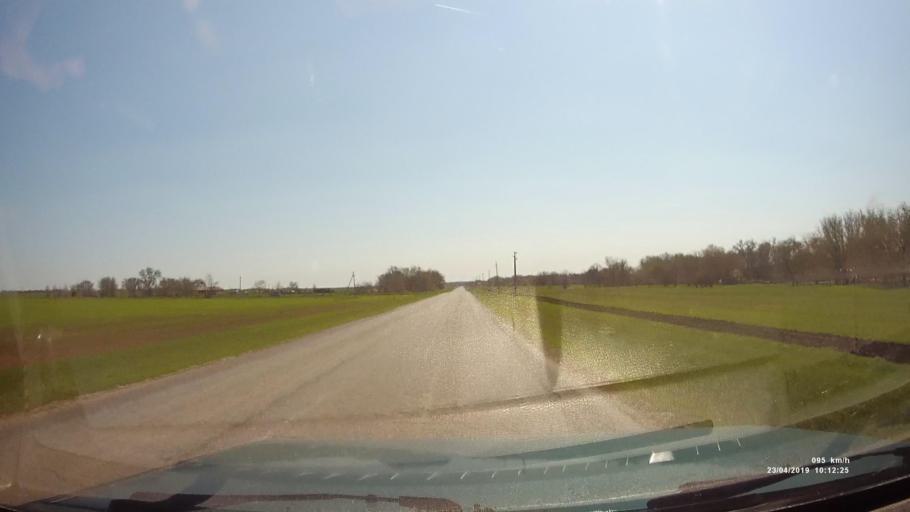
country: RU
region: Rostov
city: Sovetskoye
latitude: 46.6902
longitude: 42.3353
